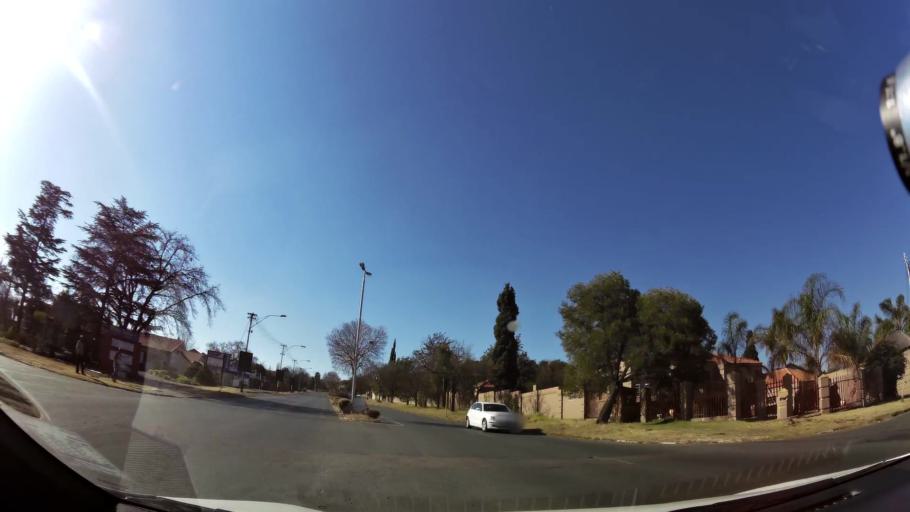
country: ZA
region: Gauteng
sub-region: City of Johannesburg Metropolitan Municipality
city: Johannesburg
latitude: -26.2766
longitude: 28.0111
